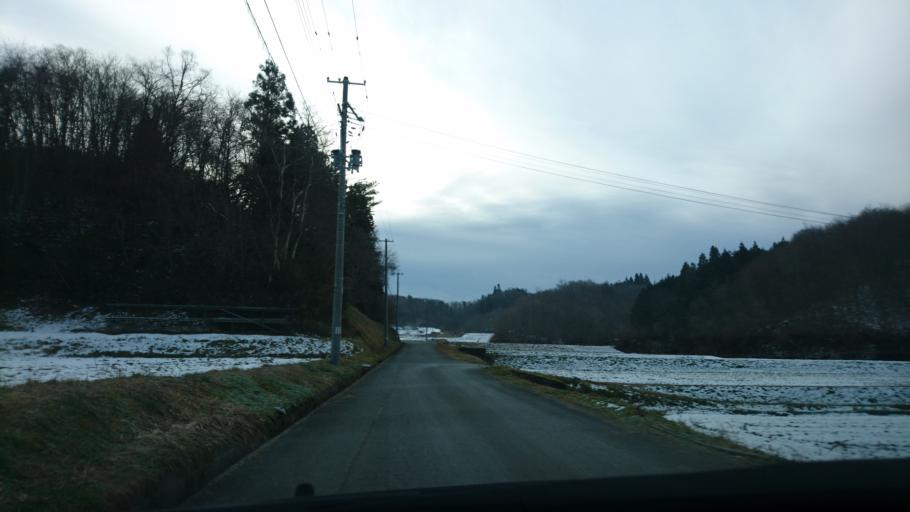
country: JP
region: Iwate
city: Ichinoseki
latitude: 38.9056
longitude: 141.3446
